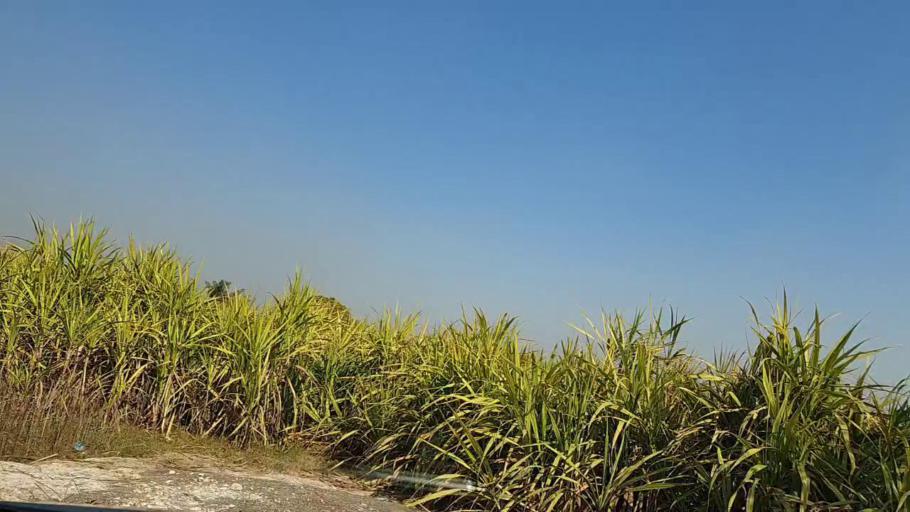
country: PK
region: Sindh
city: Nawabshah
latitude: 26.2320
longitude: 68.3112
